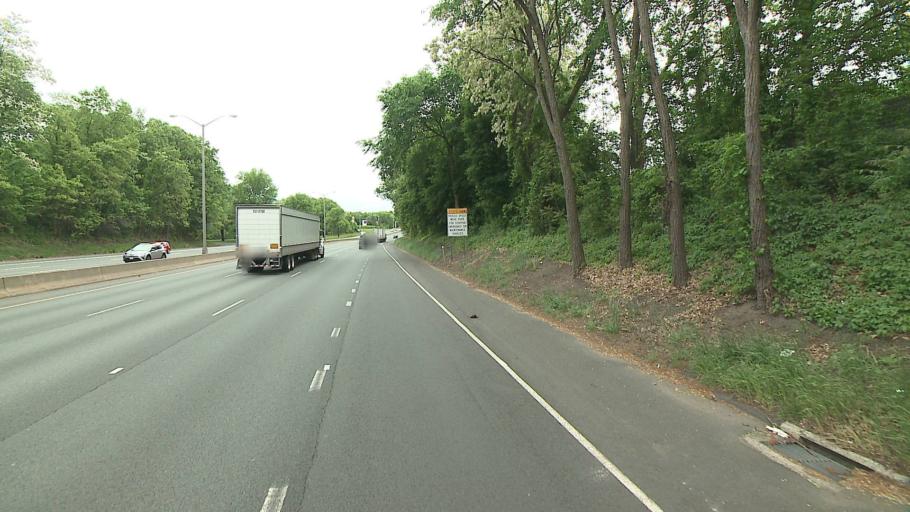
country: US
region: Connecticut
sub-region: Hartford County
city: Sherwood Manor
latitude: 42.0205
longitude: -72.5881
